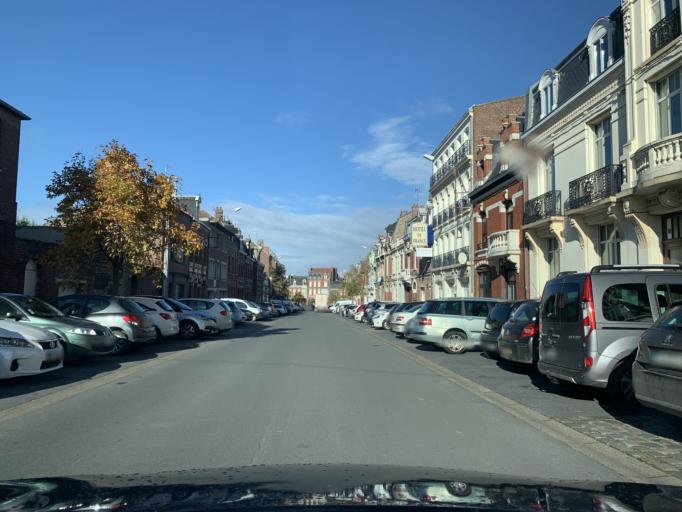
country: FR
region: Nord-Pas-de-Calais
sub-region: Departement du Nord
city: Cambrai
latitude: 50.1770
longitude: 3.2399
